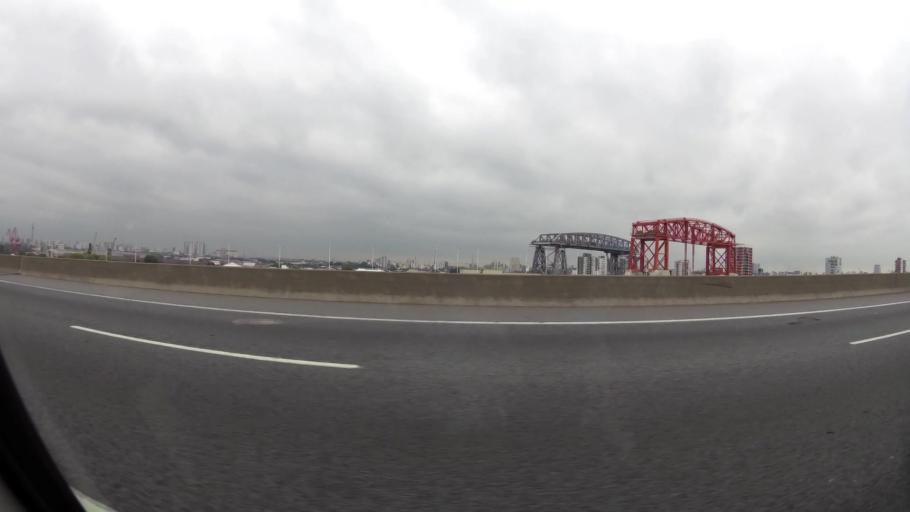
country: AR
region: Buenos Aires
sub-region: Partido de Avellaneda
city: Avellaneda
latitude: -34.6385
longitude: -58.3530
